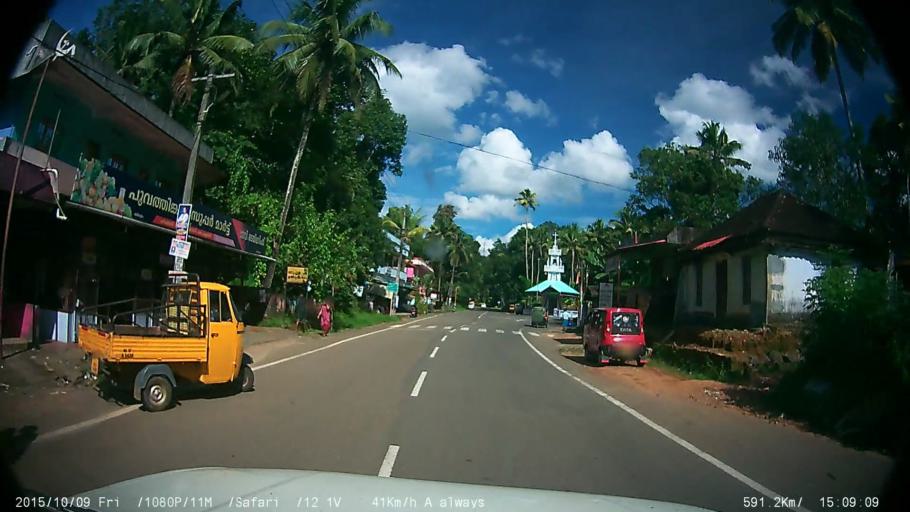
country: IN
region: Kerala
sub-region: Ernakulam
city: Piravam
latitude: 9.8863
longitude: 76.5712
